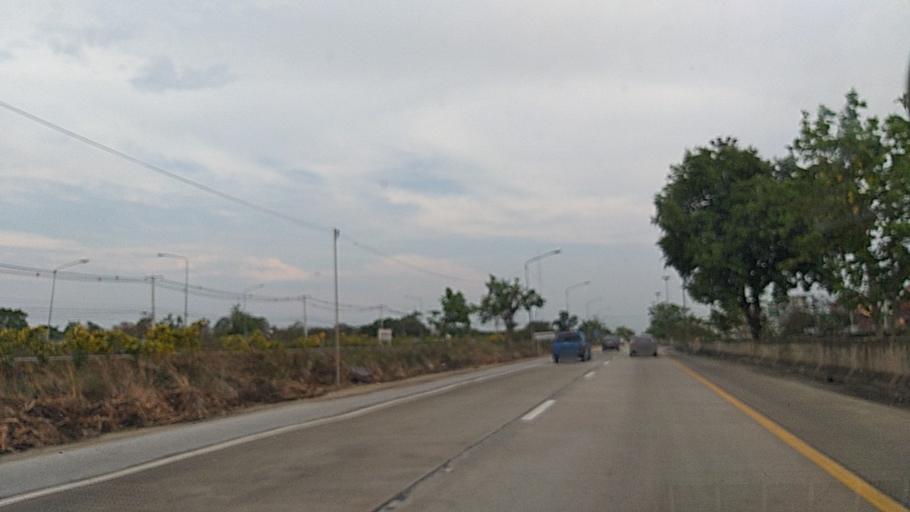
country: TH
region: Phra Nakhon Si Ayutthaya
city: Bang Pa-in
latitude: 14.1876
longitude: 100.5553
